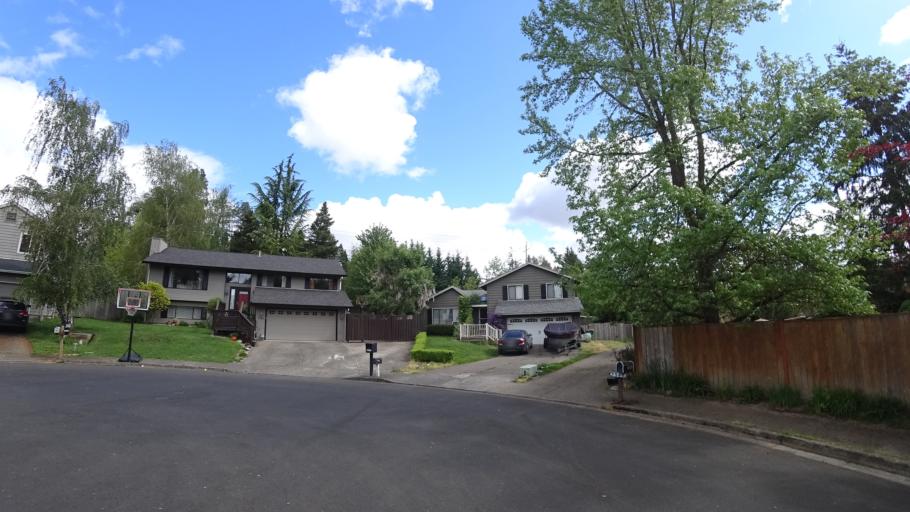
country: US
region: Oregon
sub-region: Washington County
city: Aloha
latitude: 45.4651
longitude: -122.8383
